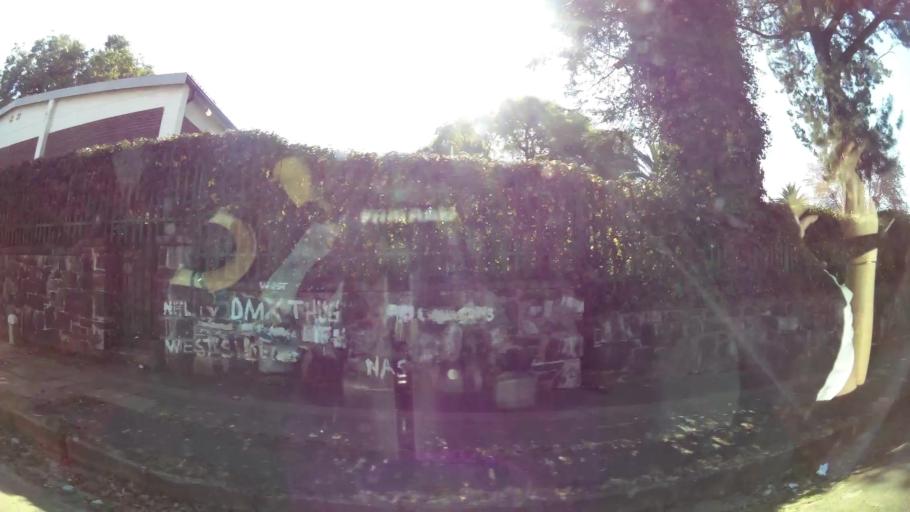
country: ZA
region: Gauteng
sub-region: City of Johannesburg Metropolitan Municipality
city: Johannesburg
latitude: -26.1897
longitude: 28.0740
